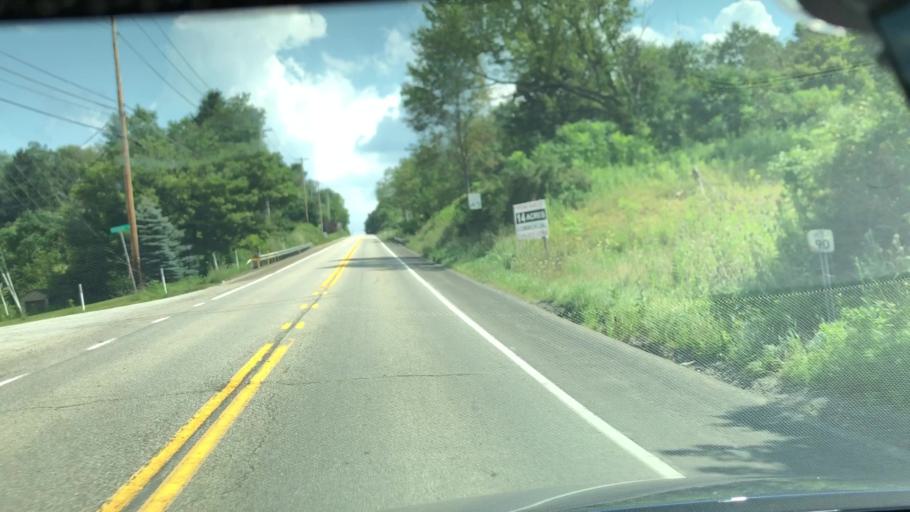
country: US
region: Pennsylvania
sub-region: Armstrong County
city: Freeport
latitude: 40.7099
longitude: -79.7344
